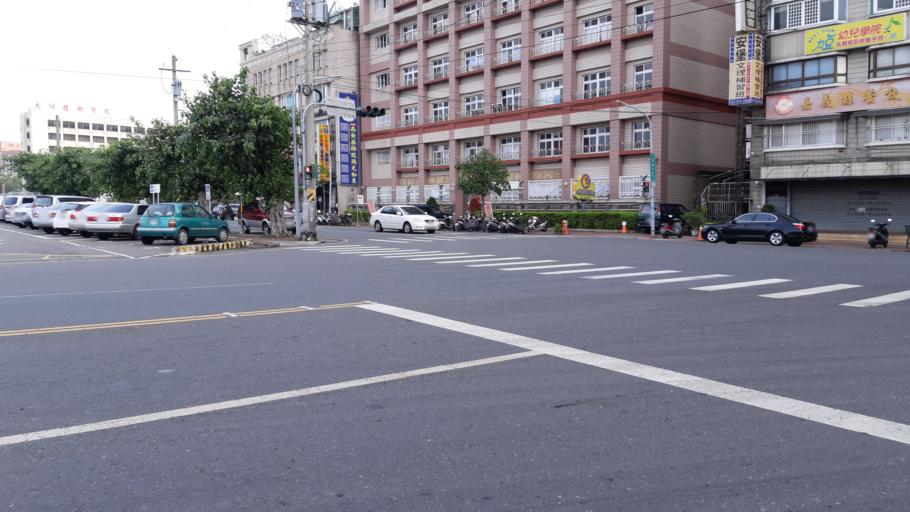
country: TW
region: Taiwan
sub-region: Chiayi
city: Jiayi Shi
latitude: 23.4703
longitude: 120.4611
